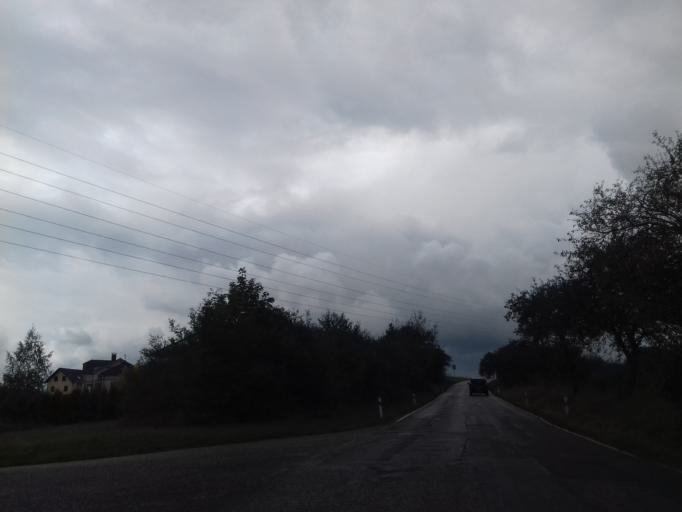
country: CZ
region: Central Bohemia
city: Revnice
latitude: 49.9256
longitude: 14.2422
